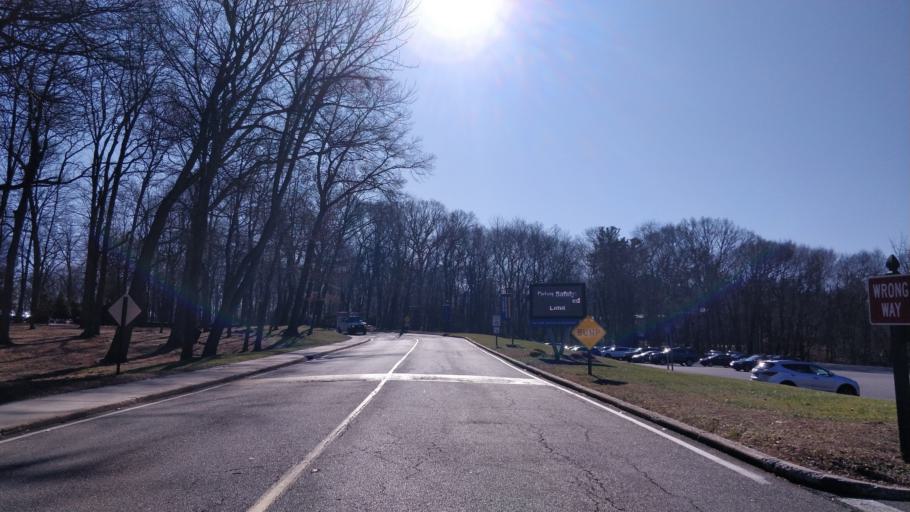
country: US
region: New York
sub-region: Nassau County
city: Old Brookville
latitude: 40.8146
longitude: -73.6071
